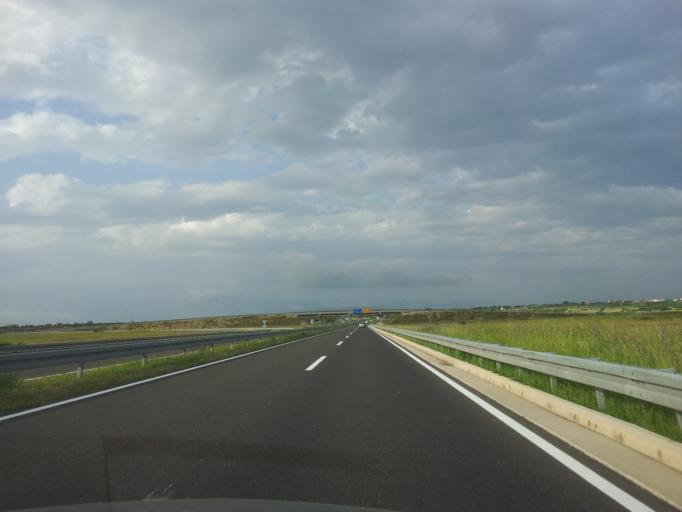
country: HR
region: Zadarska
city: Galovac
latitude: 44.1082
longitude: 15.3971
